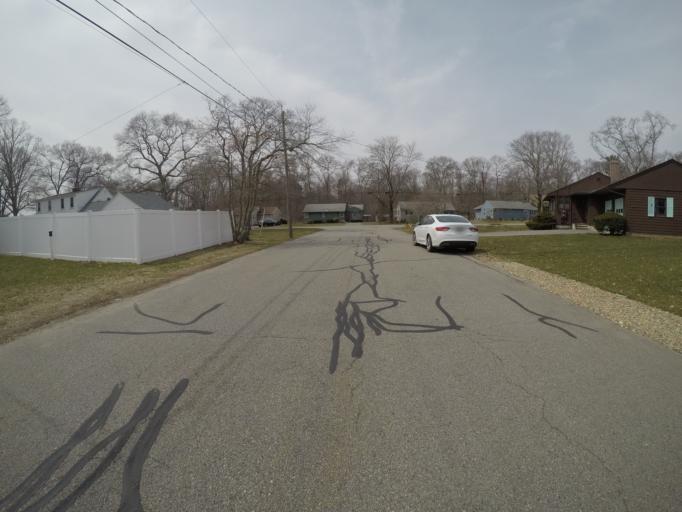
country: US
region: Massachusetts
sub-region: Bristol County
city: Easton
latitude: 42.0603
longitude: -71.1099
